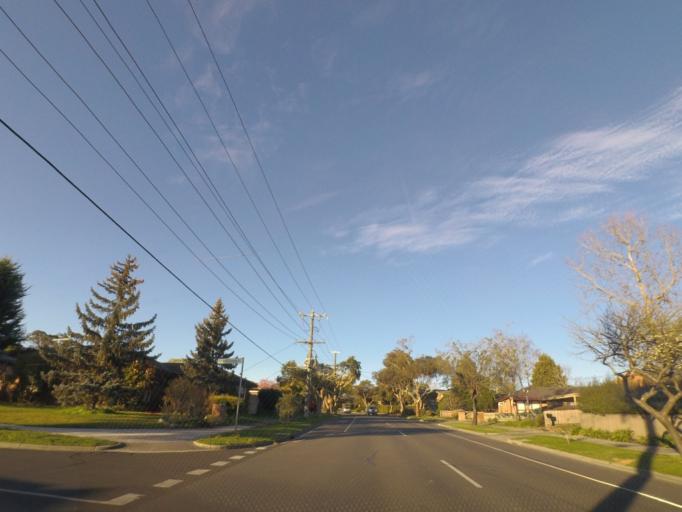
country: AU
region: Victoria
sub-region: Maroondah
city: Warranwood
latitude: -37.7874
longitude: 145.2380
